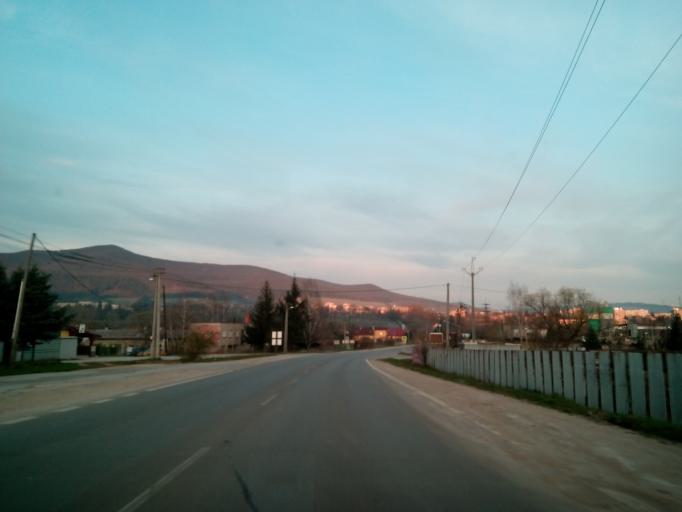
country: SK
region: Kosicky
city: Roznava
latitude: 48.6608
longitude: 20.5139
